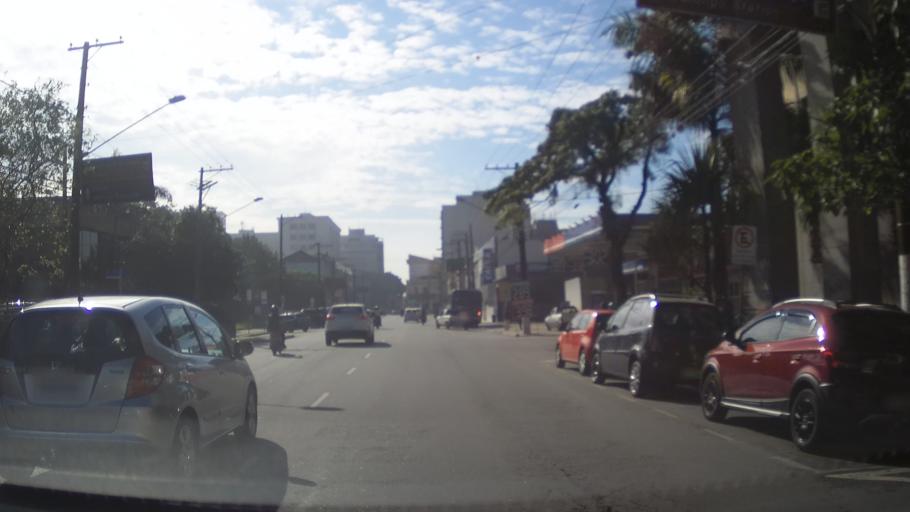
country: BR
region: Sao Paulo
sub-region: Santos
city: Santos
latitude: -23.9371
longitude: -46.3276
